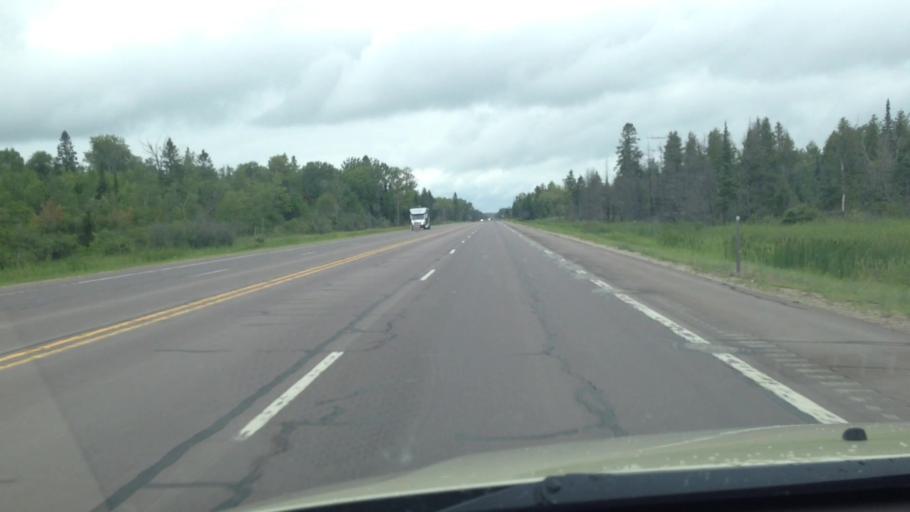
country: US
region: Michigan
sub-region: Schoolcraft County
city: Manistique
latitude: 46.0117
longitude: -85.9943
